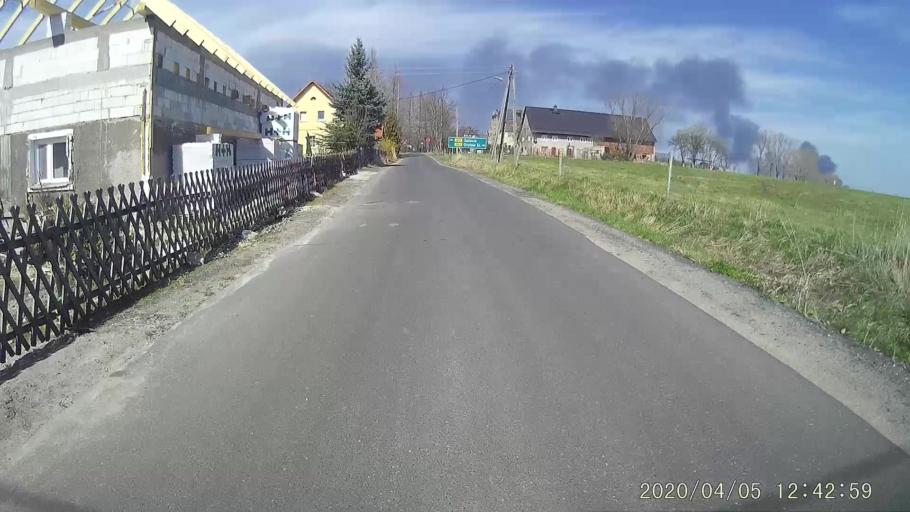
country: PL
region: Lower Silesian Voivodeship
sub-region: Powiat lwowecki
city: Mirsk
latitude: 50.9883
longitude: 15.3378
